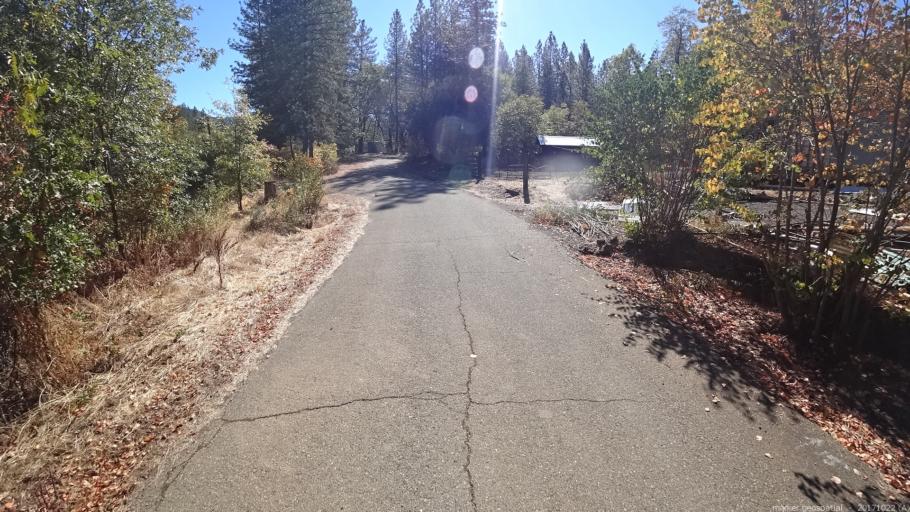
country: US
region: California
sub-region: Shasta County
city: Central Valley (historical)
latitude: 40.9073
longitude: -122.3809
